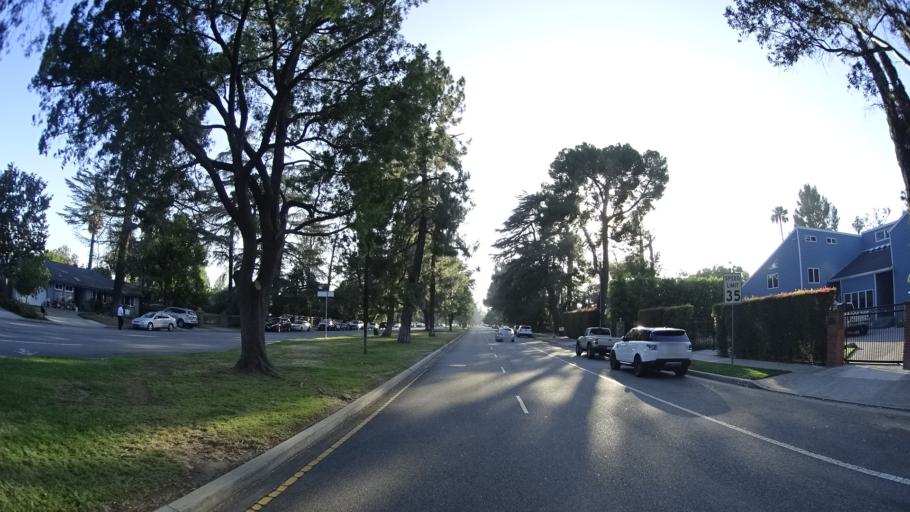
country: US
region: California
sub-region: Los Angeles County
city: Sherman Oaks
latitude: 34.1686
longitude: -118.4406
